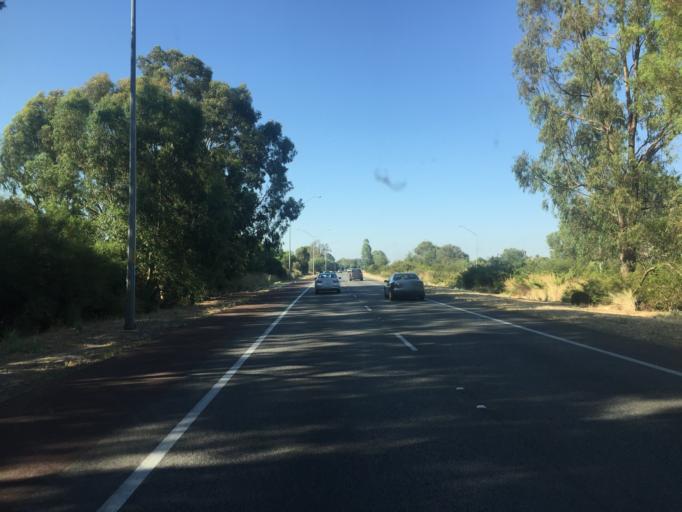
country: AU
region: Western Australia
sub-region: Canning
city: East Cannington
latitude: -32.0140
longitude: 115.9717
